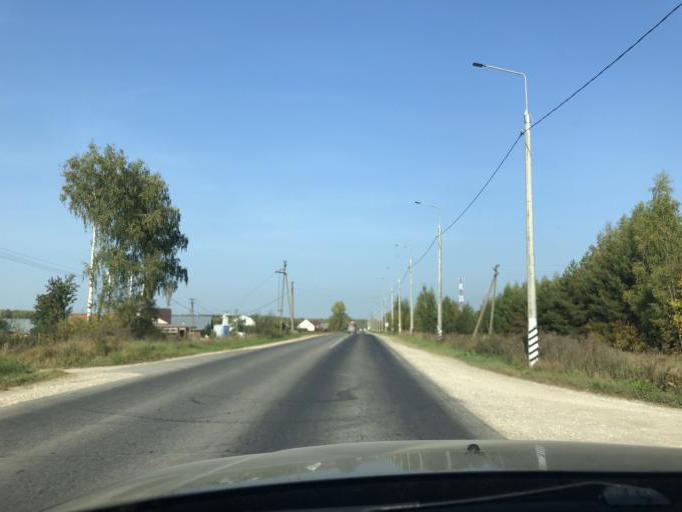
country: RU
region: Tula
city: Leninskiy
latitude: 54.2960
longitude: 37.4531
